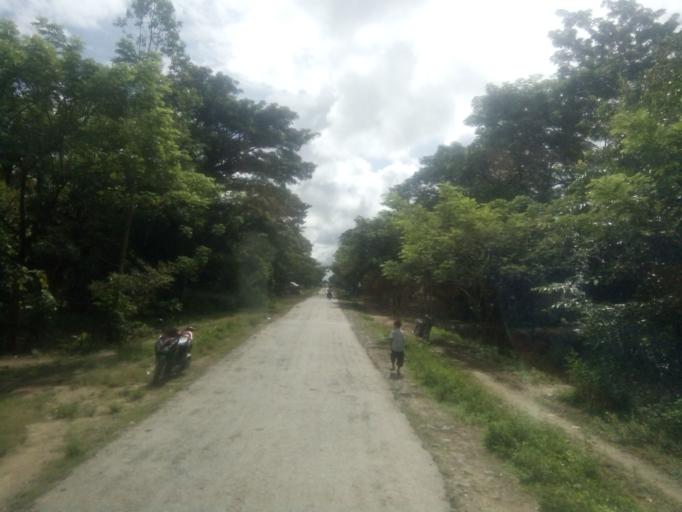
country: MM
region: Bago
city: Nyaunglebin
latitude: 17.9023
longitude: 96.5451
